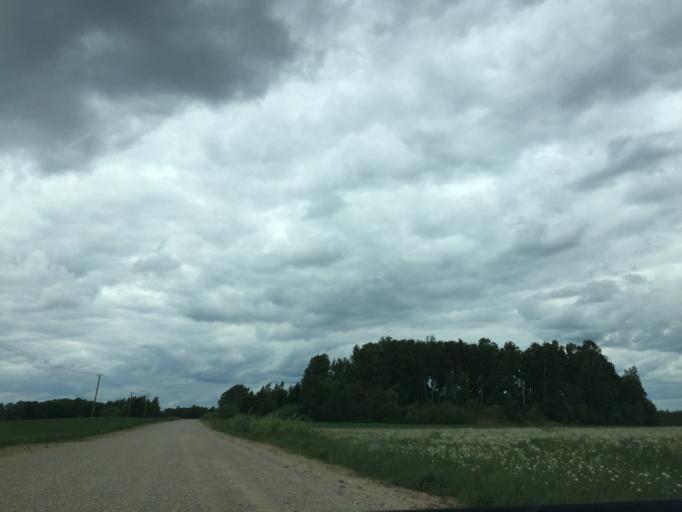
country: LV
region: Dagda
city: Dagda
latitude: 55.9826
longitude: 27.6062
